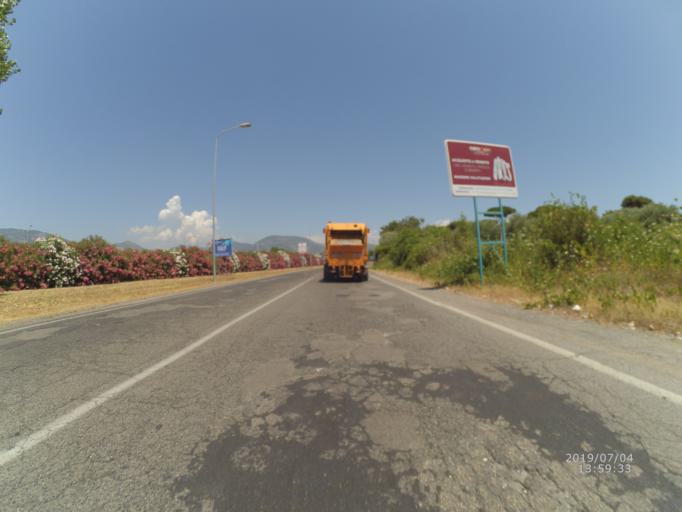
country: IT
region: Latium
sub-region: Provincia di Latina
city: Terracina
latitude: 41.2873
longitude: 13.2153
